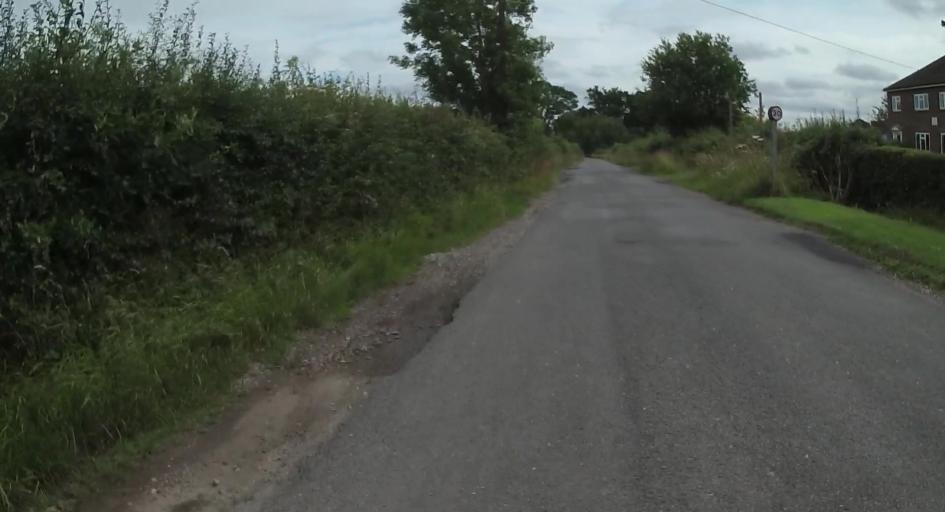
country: GB
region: England
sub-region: West Berkshire
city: Stratfield Mortimer
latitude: 51.3480
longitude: -1.0424
